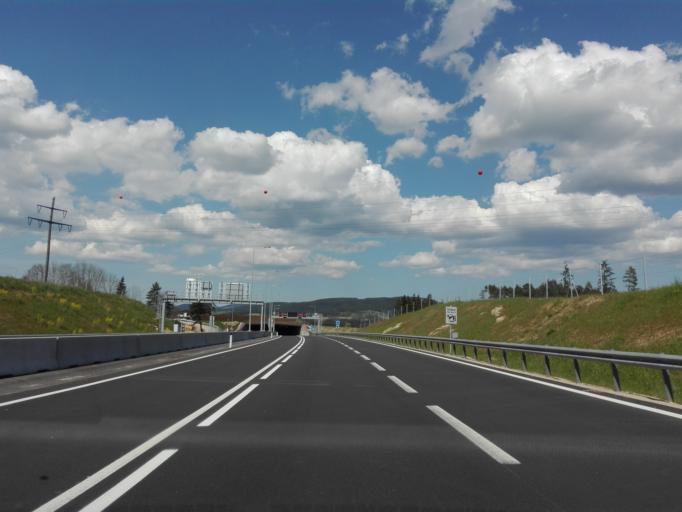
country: AT
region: Upper Austria
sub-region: Politischer Bezirk Freistadt
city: Freistadt
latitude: 48.4492
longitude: 14.4948
